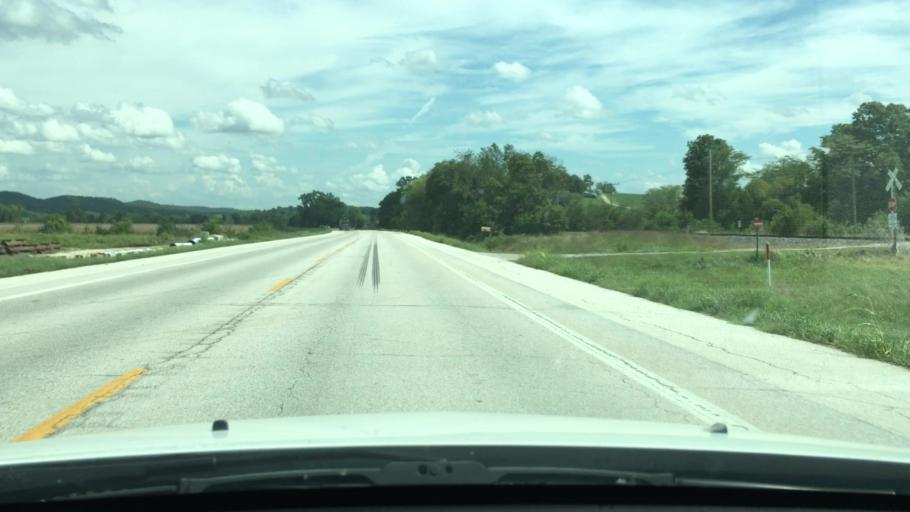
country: US
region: Missouri
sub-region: Pike County
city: Bowling Green
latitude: 39.3833
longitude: -91.1298
